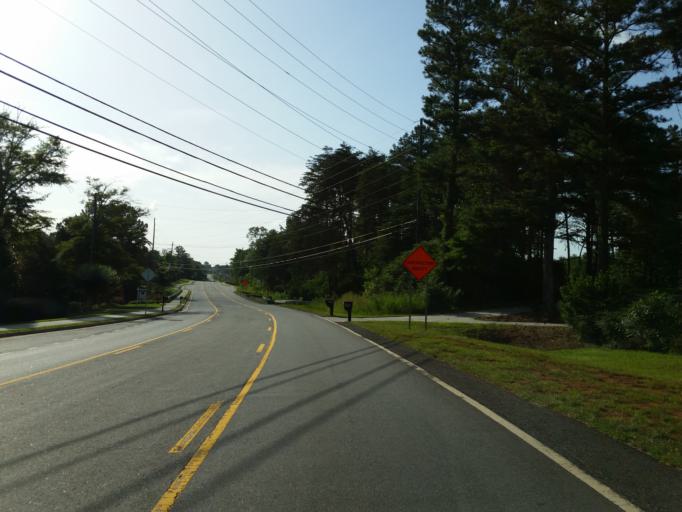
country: US
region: Georgia
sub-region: Cherokee County
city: Woodstock
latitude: 34.0676
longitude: -84.4710
